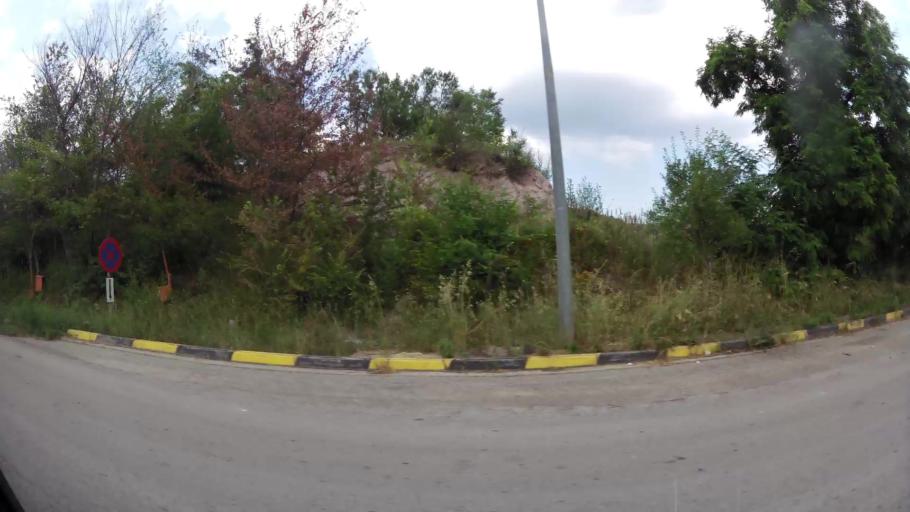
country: GR
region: West Macedonia
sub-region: Nomos Kozanis
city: Koila
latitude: 40.3365
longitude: 21.8255
